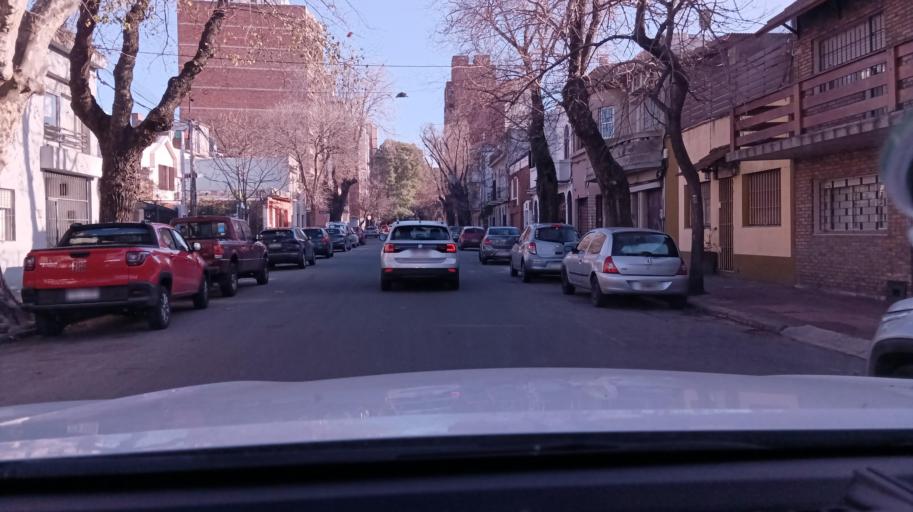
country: UY
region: Montevideo
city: Montevideo
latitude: -34.9046
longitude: -56.1485
